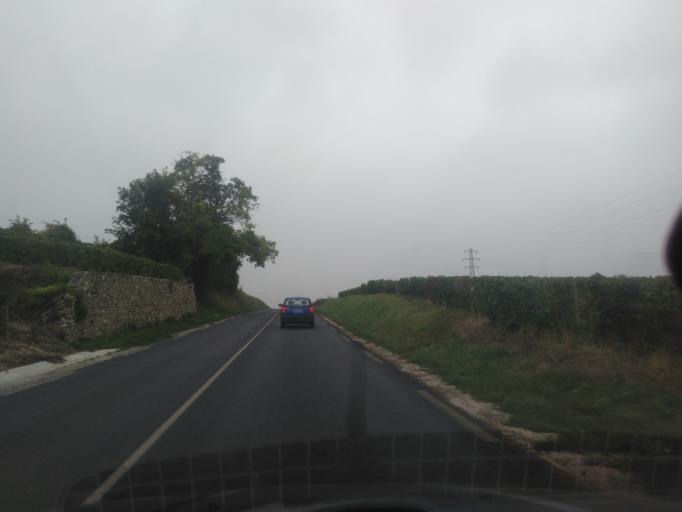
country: FR
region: Champagne-Ardenne
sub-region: Departement de la Marne
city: Damery
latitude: 49.0705
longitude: 3.8891
